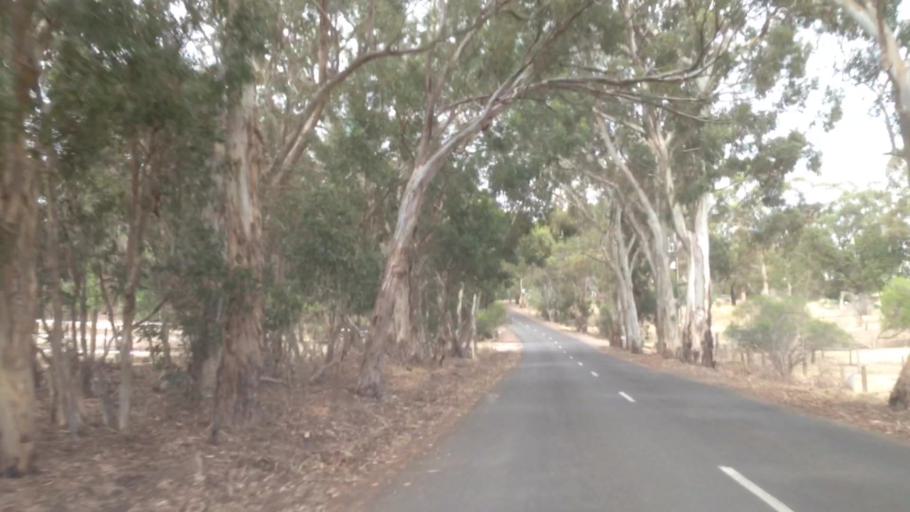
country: AU
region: South Australia
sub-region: Barossa
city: Williamstown
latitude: -34.6427
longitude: 138.8530
